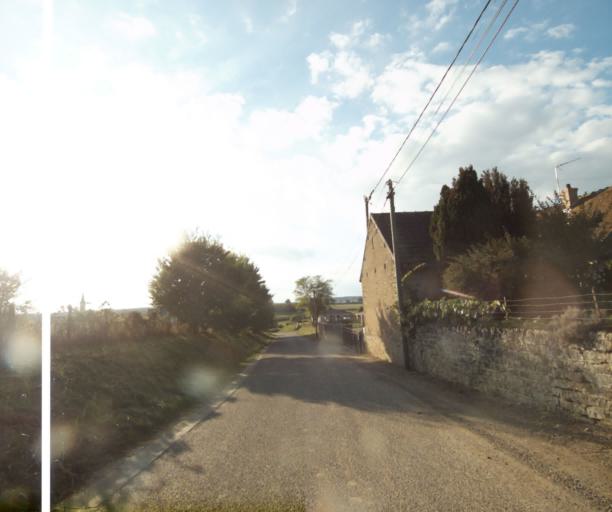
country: FR
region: Bourgogne
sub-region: Departement de Saone-et-Loire
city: Palinges
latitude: 46.5762
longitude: 4.1623
